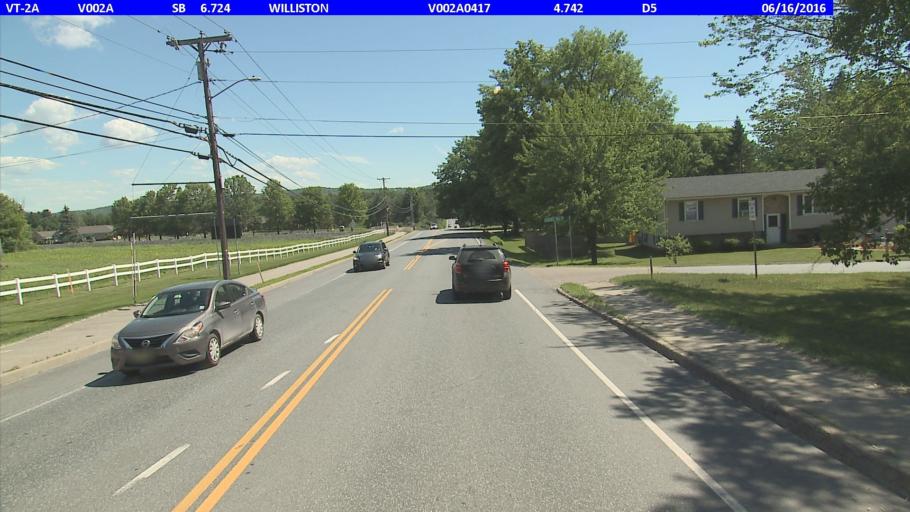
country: US
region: Vermont
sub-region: Chittenden County
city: Essex Junction
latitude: 44.4643
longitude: -73.1128
